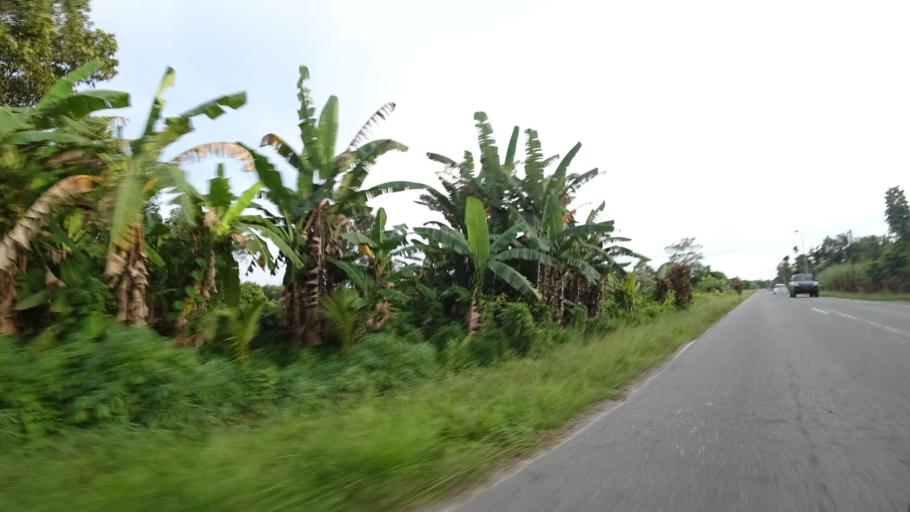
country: BN
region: Tutong
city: Tutong
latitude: 4.8264
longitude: 114.8186
